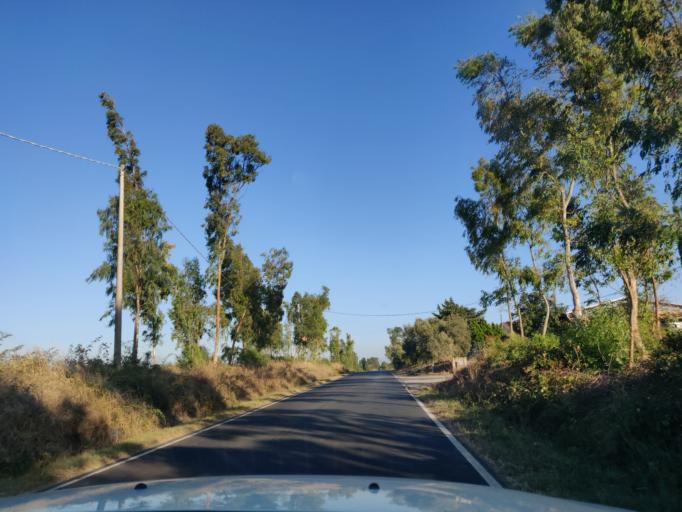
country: IT
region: Latium
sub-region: Provincia di Viterbo
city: Montalto di Castro
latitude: 42.2896
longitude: 11.6596
